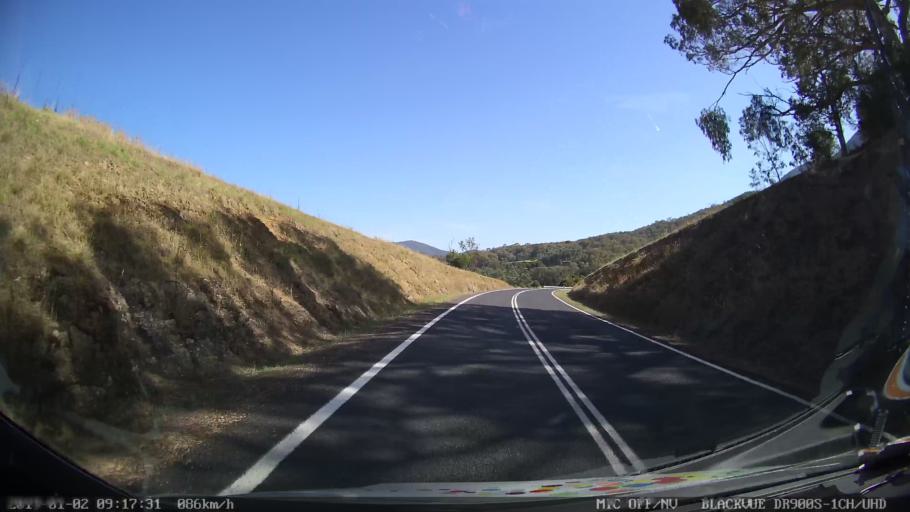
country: AU
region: New South Wales
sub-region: Tumut Shire
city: Tumut
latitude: -35.4392
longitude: 148.2864
